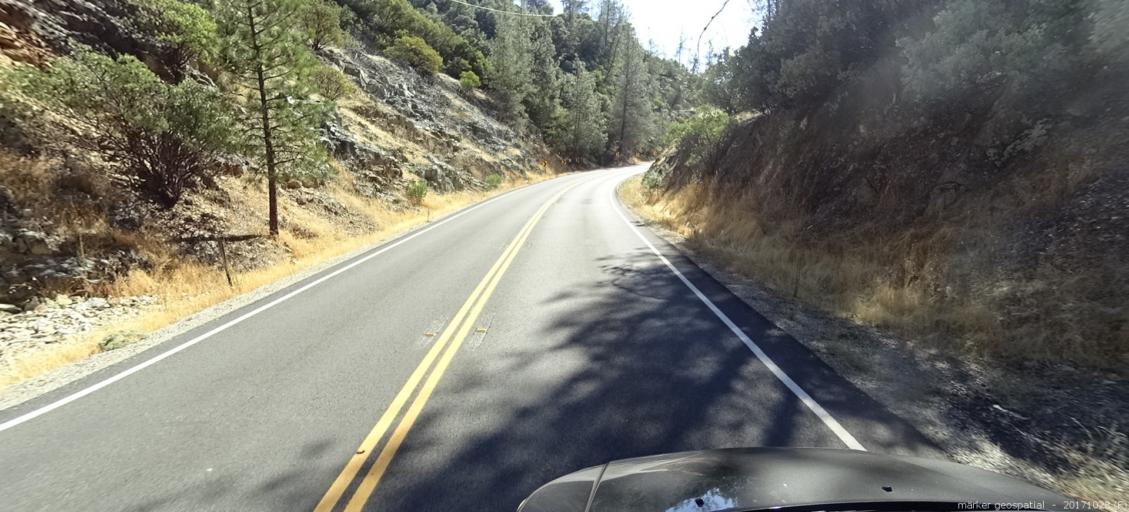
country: US
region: California
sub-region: Shasta County
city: Shasta
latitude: 40.6013
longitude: -122.5354
